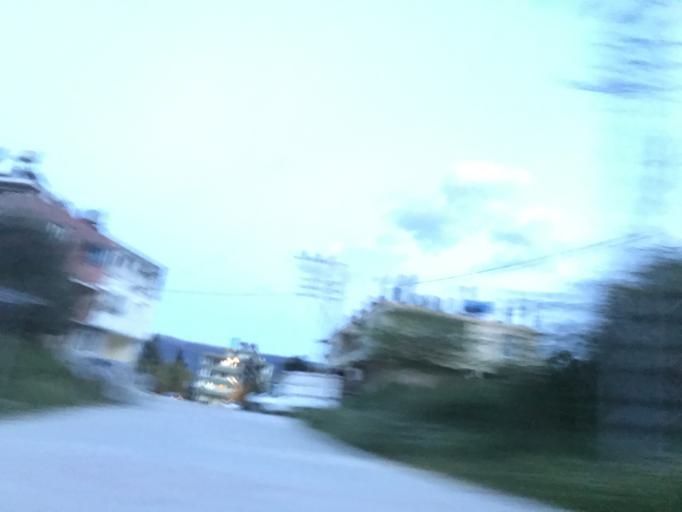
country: TR
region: Hatay
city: Karacay
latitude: 36.1507
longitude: 36.0905
